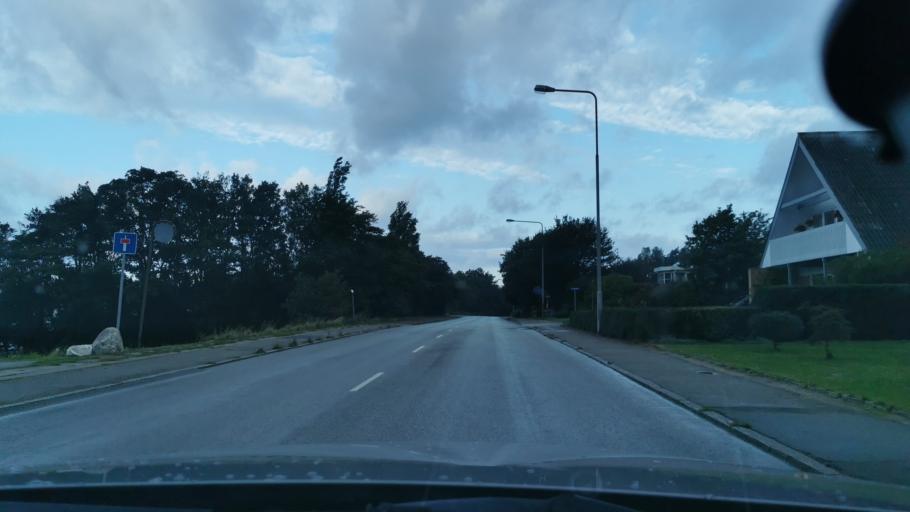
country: DK
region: Zealand
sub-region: Kalundborg Kommune
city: Kalundborg
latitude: 55.7005
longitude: 11.0321
